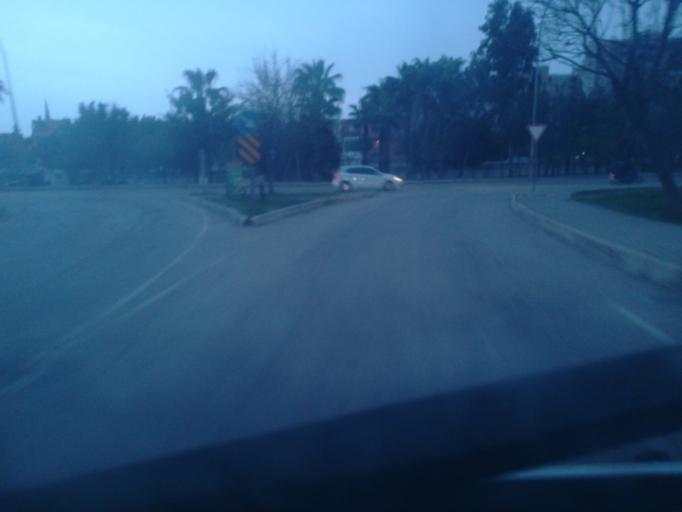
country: TR
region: Adana
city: Seyhan
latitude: 37.0126
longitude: 35.2821
